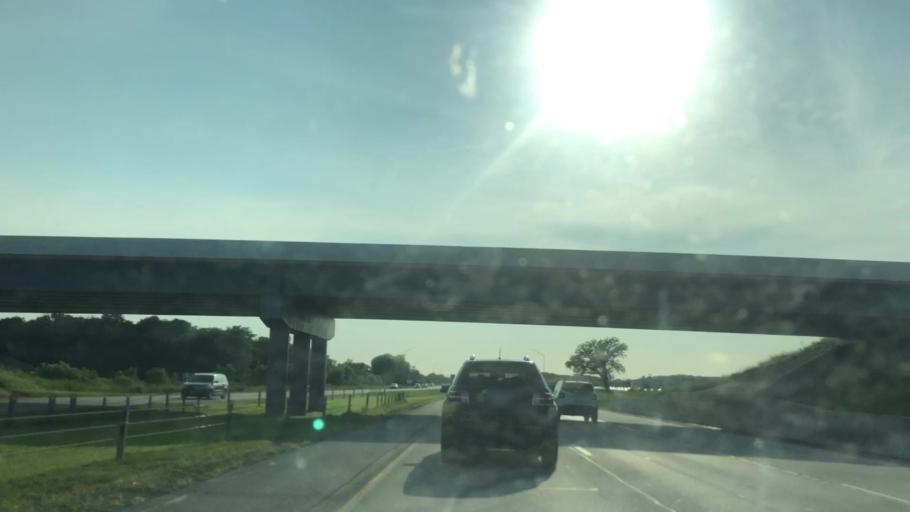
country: US
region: Iowa
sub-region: Story County
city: Ames
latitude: 42.0067
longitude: -93.5861
